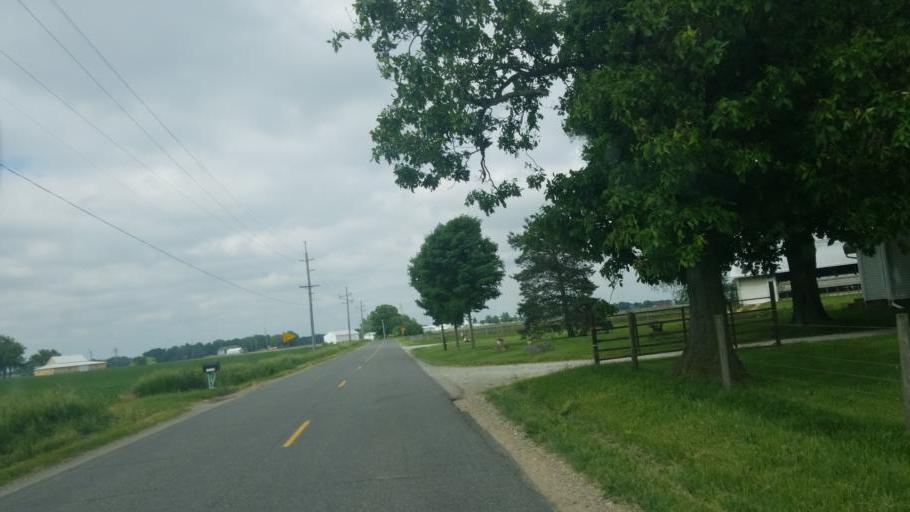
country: US
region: Indiana
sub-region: Elkhart County
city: Wakarusa
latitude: 41.4898
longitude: -86.0292
